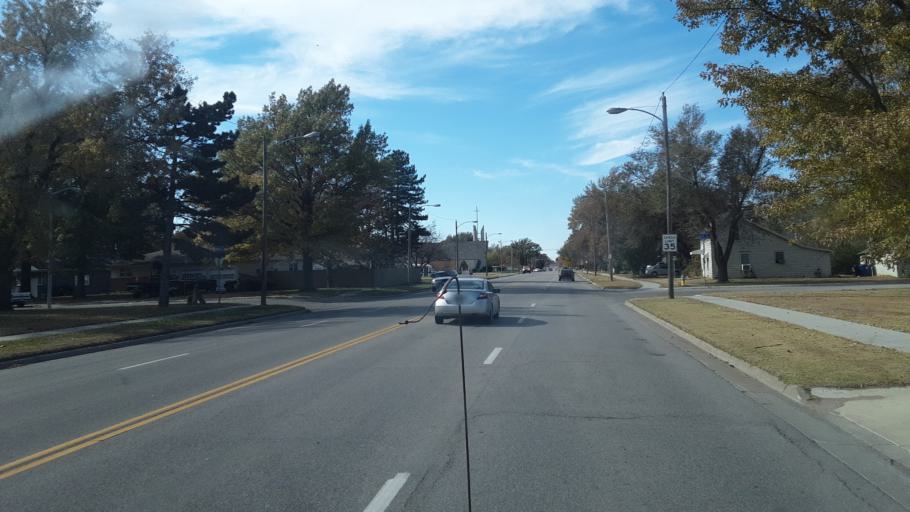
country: US
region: Kansas
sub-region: McPherson County
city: McPherson
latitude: 38.3695
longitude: -97.6441
